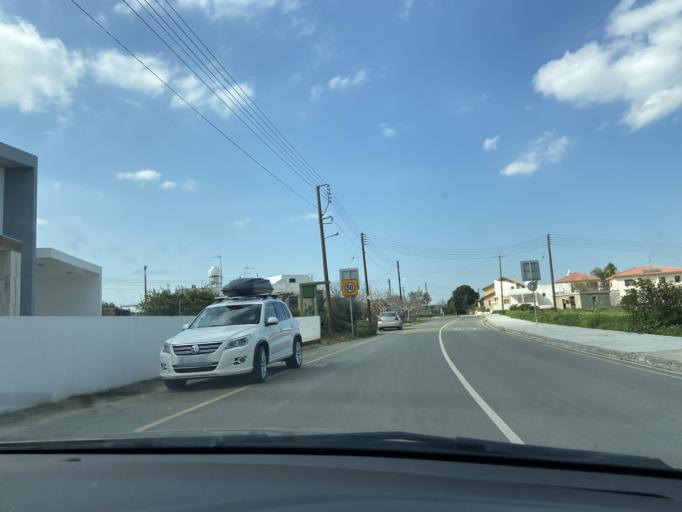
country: CY
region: Lefkosia
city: Alampra
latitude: 35.0209
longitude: 33.3876
